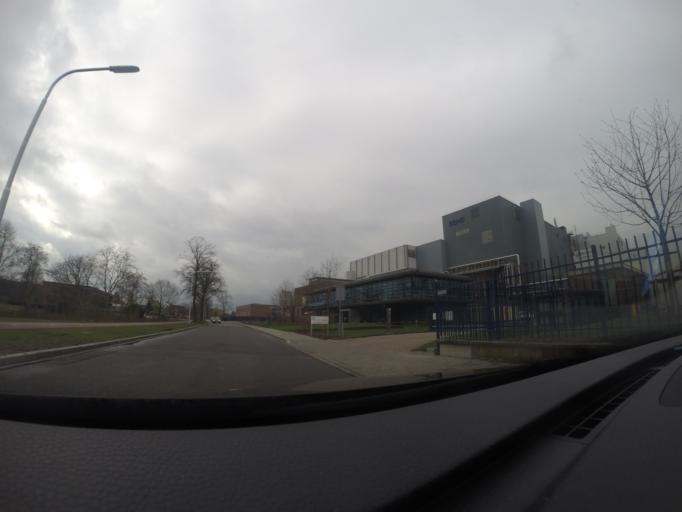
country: NL
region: Gelderland
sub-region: Berkelland
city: Borculo
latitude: 52.1178
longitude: 6.5293
